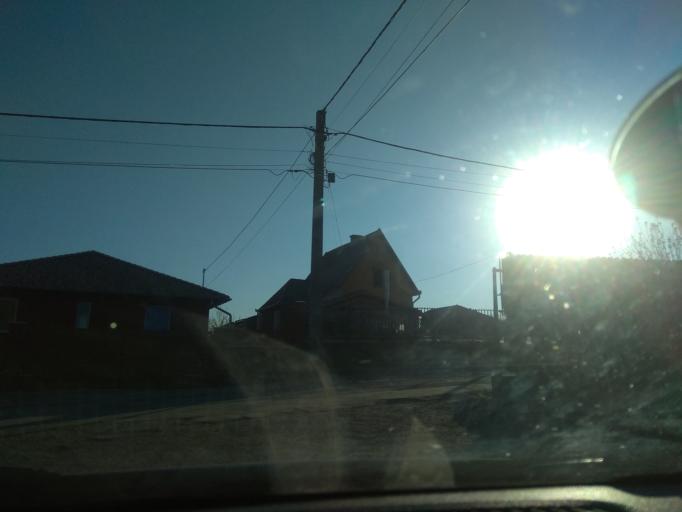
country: HU
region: Pest
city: Szigethalom
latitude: 47.3206
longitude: 19.0263
